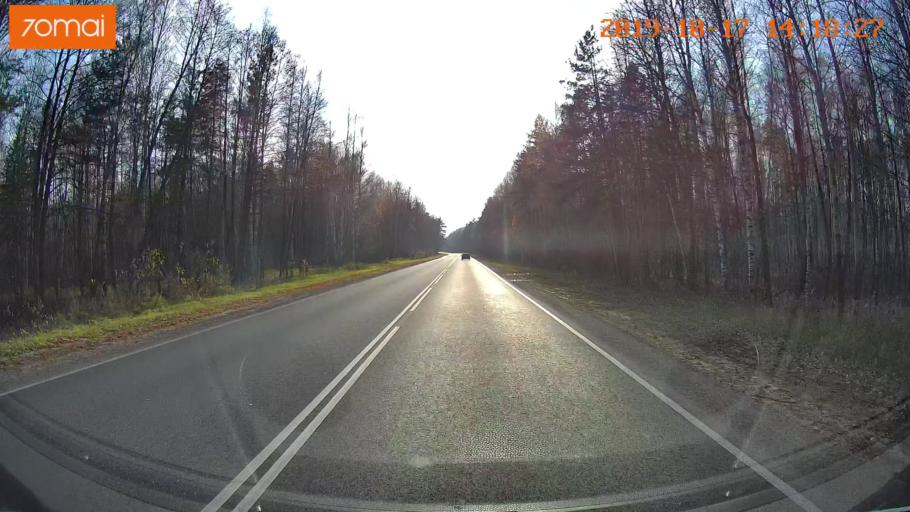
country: RU
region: Rjazan
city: Spas-Klepiki
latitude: 55.0628
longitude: 40.0303
